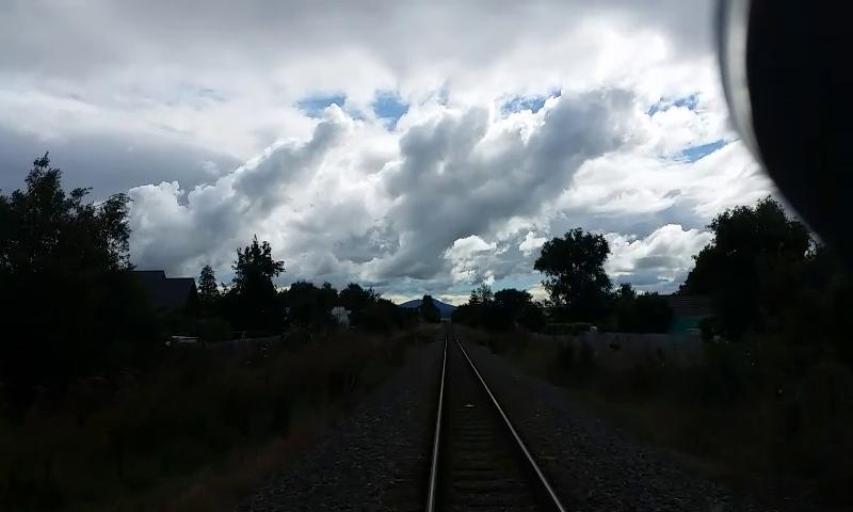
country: NZ
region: Canterbury
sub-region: Waimakariri District
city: Woodend
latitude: -43.3101
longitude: 172.6000
